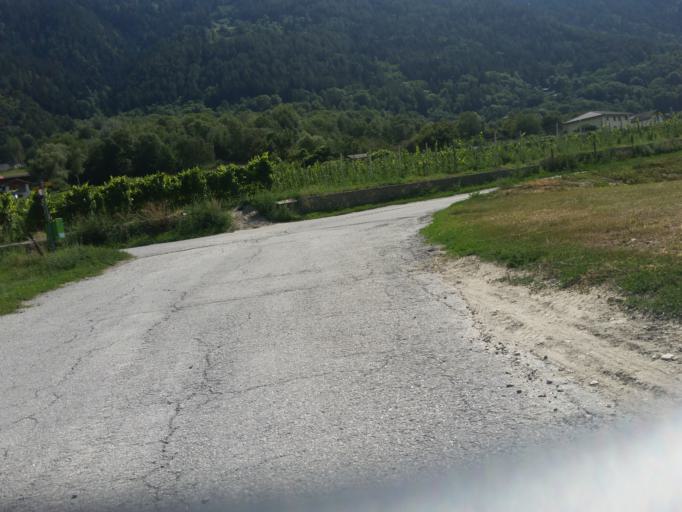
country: CH
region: Valais
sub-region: Leuk District
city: Turtmann
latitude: 46.2978
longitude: 7.6737
